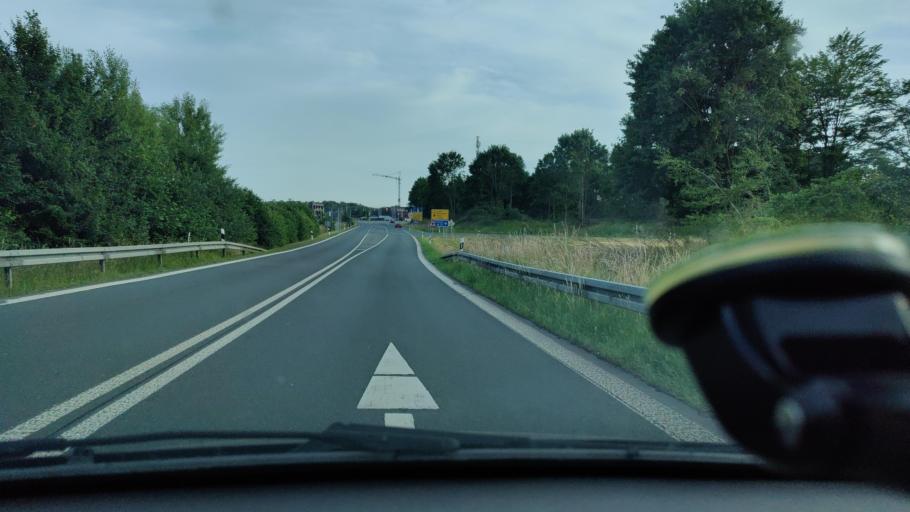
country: DE
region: North Rhine-Westphalia
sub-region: Regierungsbezirk Munster
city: Legden
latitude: 52.0534
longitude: 7.0647
